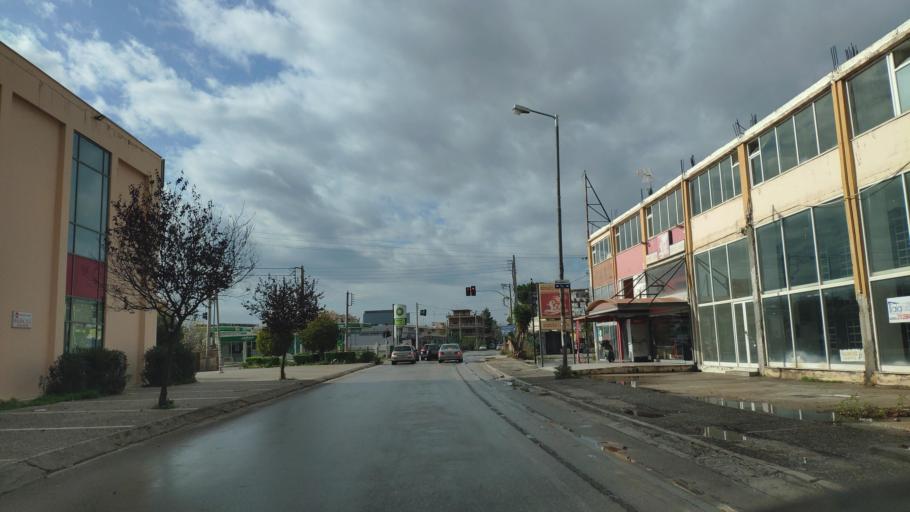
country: GR
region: Attica
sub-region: Nomarchia Dytikis Attikis
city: Elefsina
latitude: 38.0464
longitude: 23.5492
